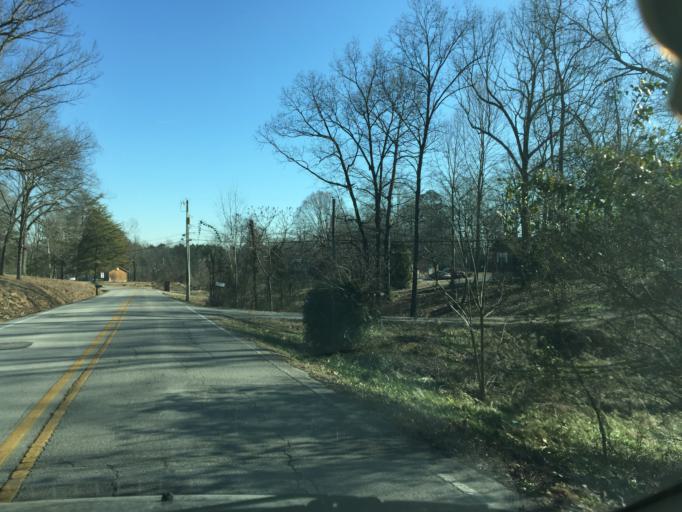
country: US
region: Tennessee
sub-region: Hamilton County
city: Collegedale
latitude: 35.0634
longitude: -85.1013
